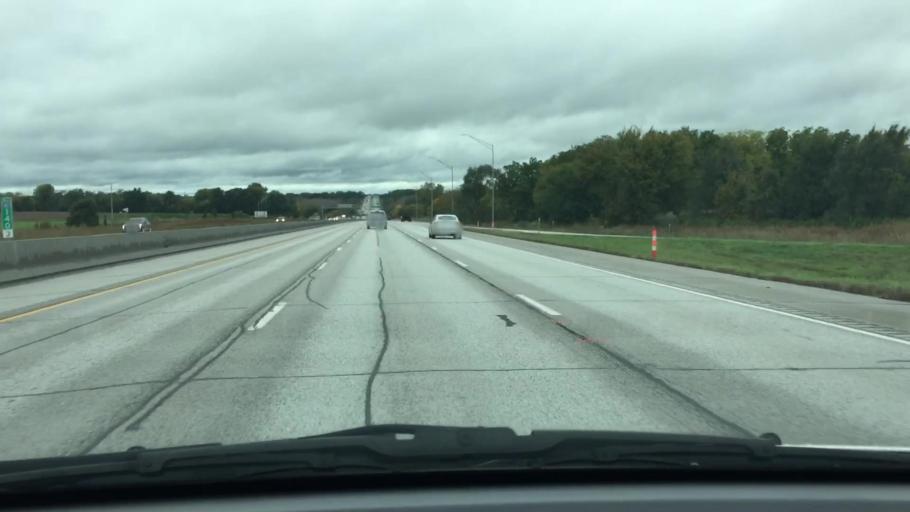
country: US
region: Iowa
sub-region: Polk County
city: Altoona
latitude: 41.6589
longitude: -93.5300
